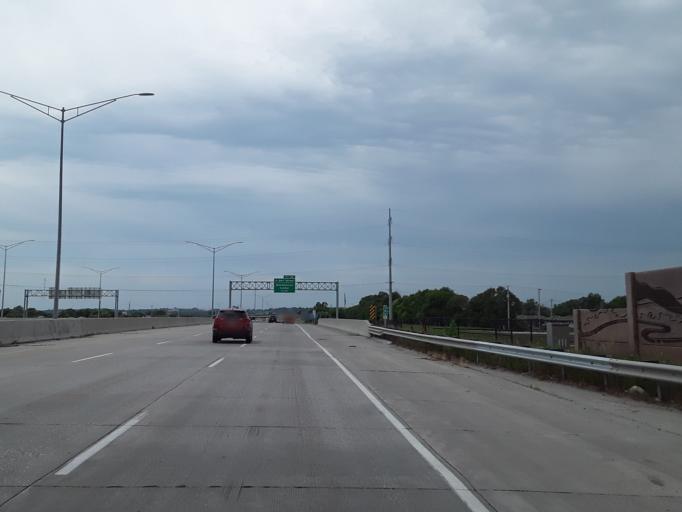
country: US
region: Iowa
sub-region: Pottawattamie County
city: Council Bluffs
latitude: 41.2327
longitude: -95.8636
